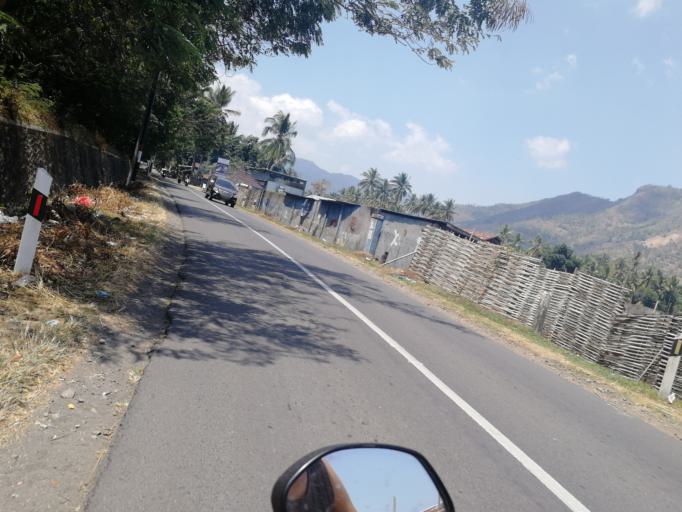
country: ID
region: West Nusa Tenggara
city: Karangsubagan
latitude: -8.4097
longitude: 116.0998
